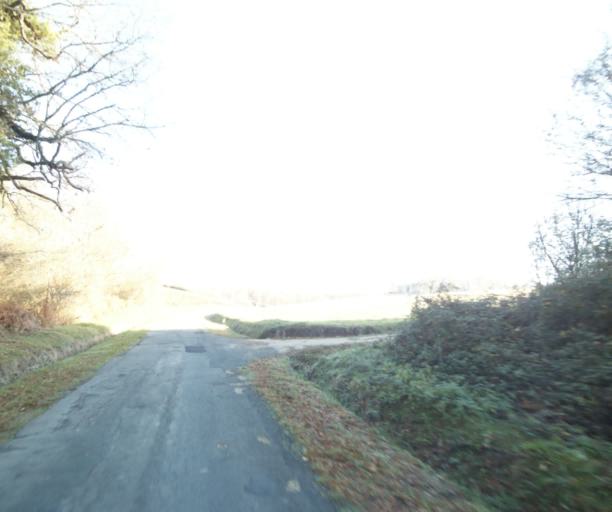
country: FR
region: Poitou-Charentes
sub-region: Departement de la Charente-Maritime
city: Burie
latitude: 45.7379
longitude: -0.4185
